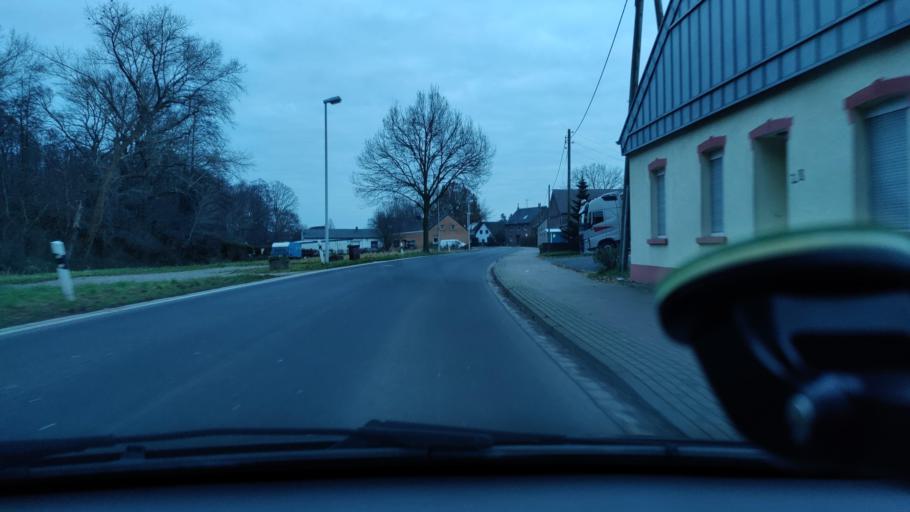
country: DE
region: North Rhine-Westphalia
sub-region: Regierungsbezirk Dusseldorf
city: Nettetal
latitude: 51.2865
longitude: 6.2831
